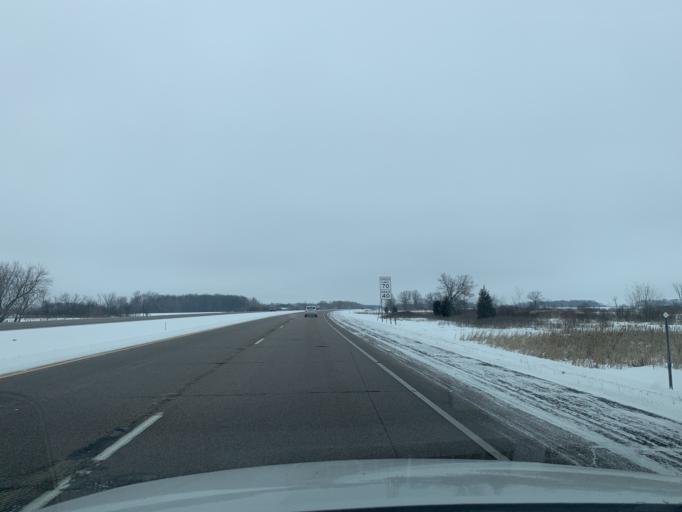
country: US
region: Minnesota
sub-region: Chisago County
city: Rush City
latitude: 45.6930
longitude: -92.9916
